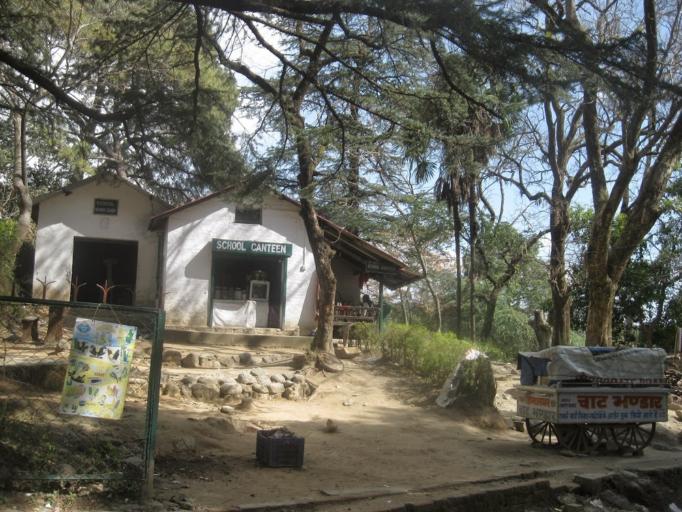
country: IN
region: Himachal Pradesh
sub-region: Kangra
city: Palampur
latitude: 32.1142
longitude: 76.5383
